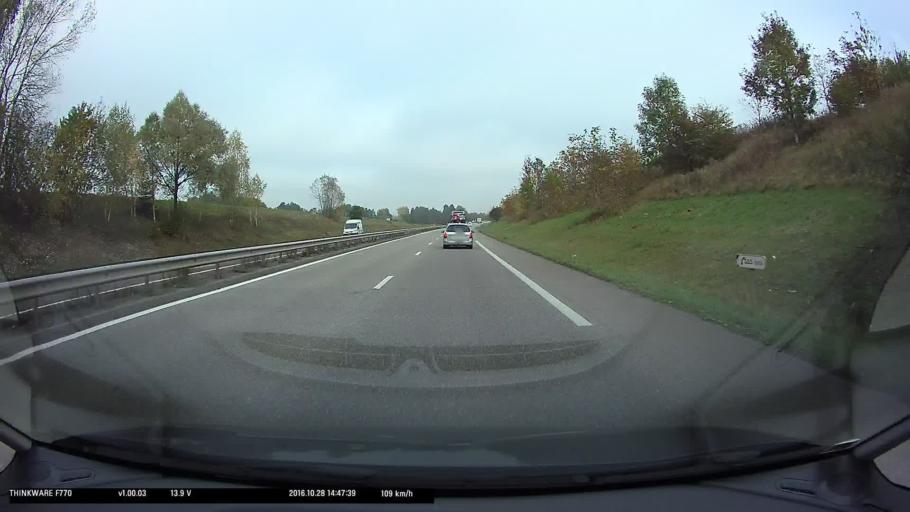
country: FR
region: Lorraine
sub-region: Departement de la Moselle
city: Sarrebourg
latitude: 48.7294
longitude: 7.0686
